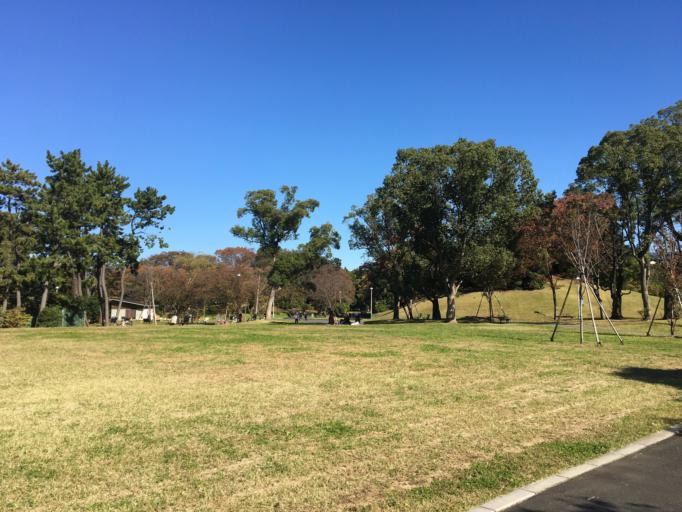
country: JP
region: Tokyo
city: Urayasu
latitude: 35.6444
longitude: 139.8096
